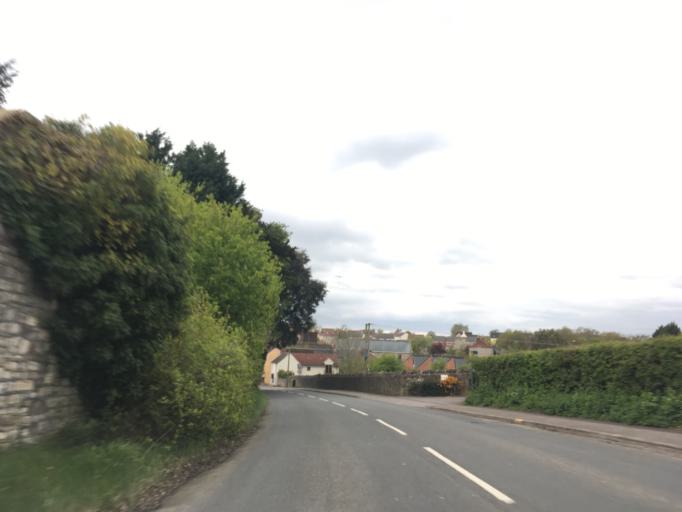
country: GB
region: England
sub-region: Gloucestershire
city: Wotton-under-Edge
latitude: 51.6286
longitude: -2.3664
